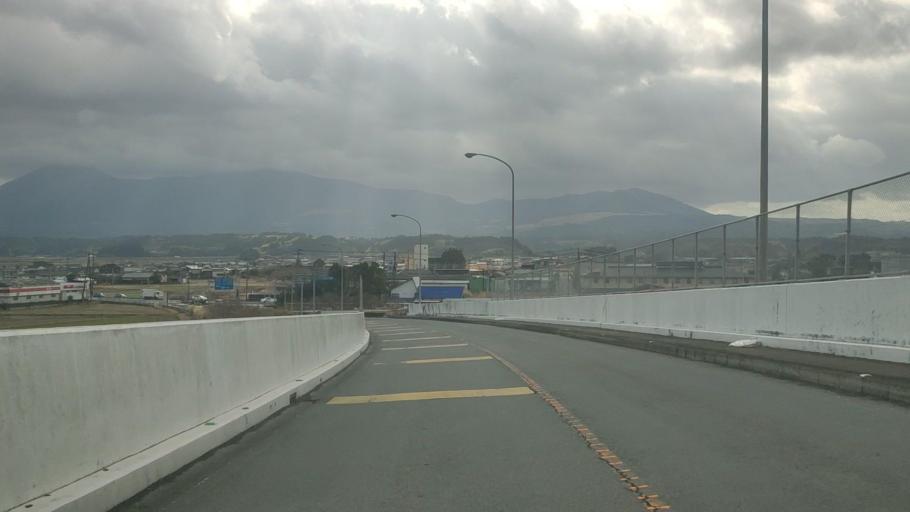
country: JP
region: Kumamoto
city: Hitoyoshi
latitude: 32.0546
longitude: 130.8170
